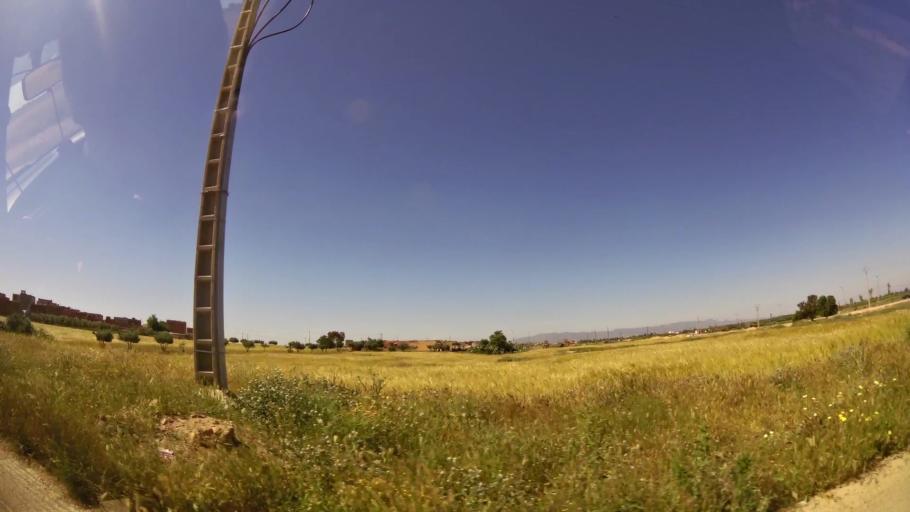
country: MA
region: Oriental
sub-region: Oujda-Angad
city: Oujda
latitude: 34.6959
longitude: -1.8579
